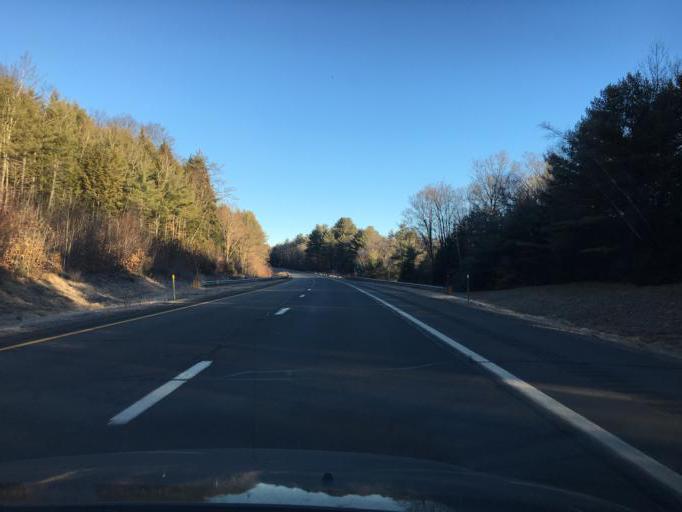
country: US
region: New Hampshire
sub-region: Belknap County
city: Sanbornton
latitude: 43.5240
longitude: -71.6122
